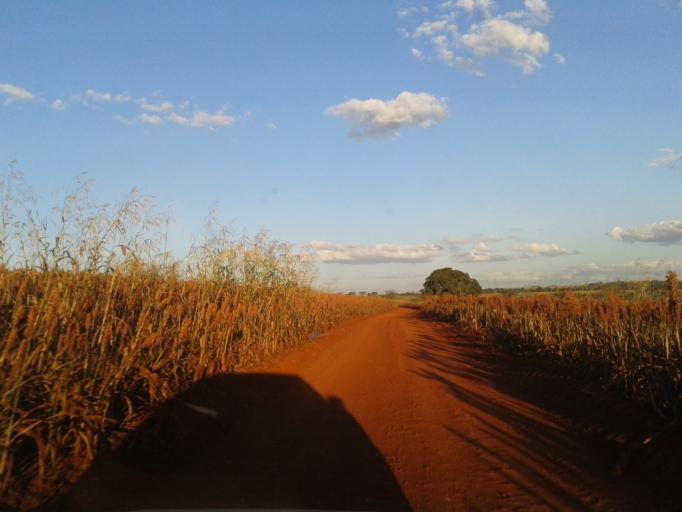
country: BR
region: Minas Gerais
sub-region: Centralina
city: Centralina
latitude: -18.6036
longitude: -49.3041
